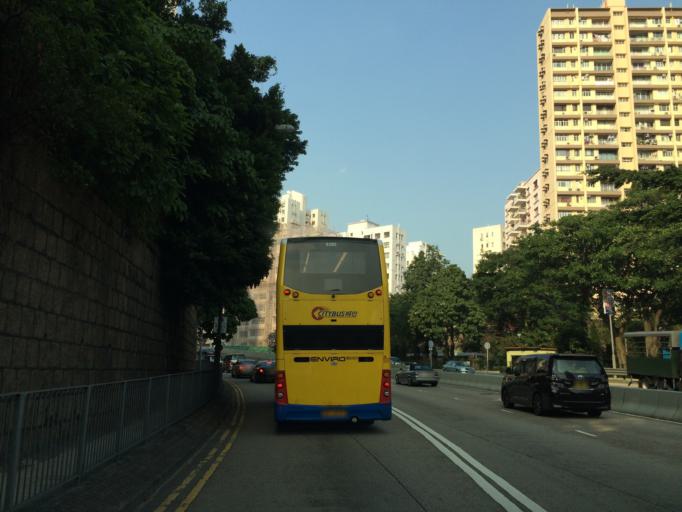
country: HK
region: Kowloon City
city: Kowloon
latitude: 22.3186
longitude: 114.1790
